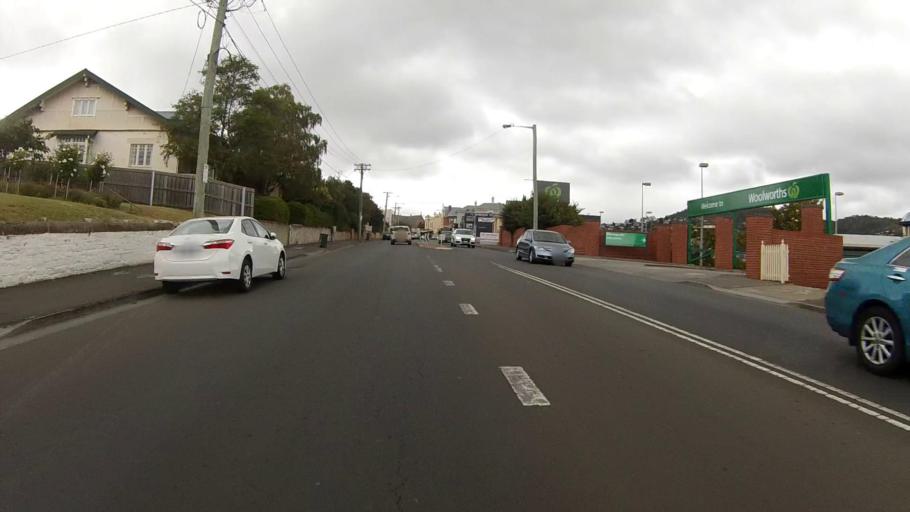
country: AU
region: Tasmania
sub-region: Hobart
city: New Town
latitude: -42.8569
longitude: 147.3039
